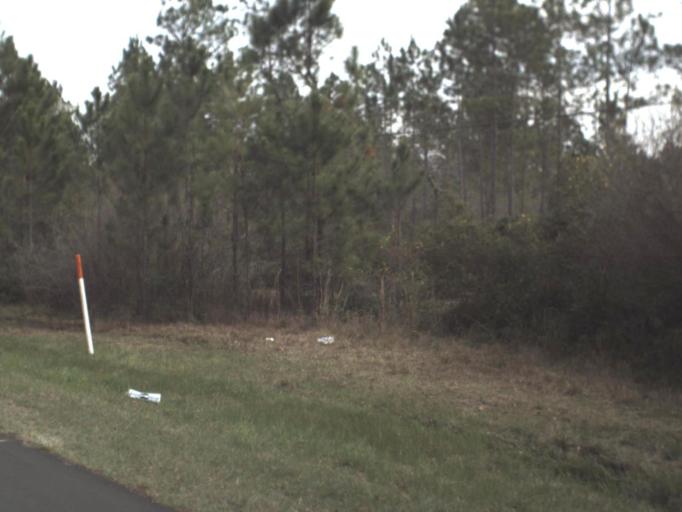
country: US
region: Florida
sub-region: Gadsden County
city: Midway
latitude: 30.3911
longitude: -84.6232
